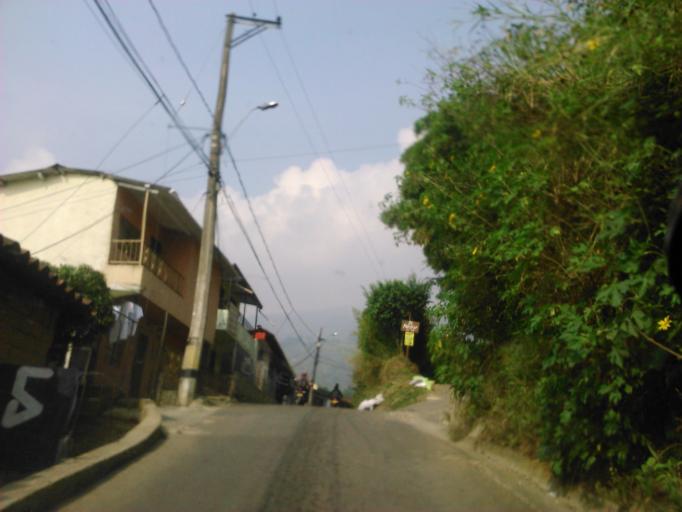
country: CO
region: Antioquia
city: La Estrella
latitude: 6.1437
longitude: -75.6387
